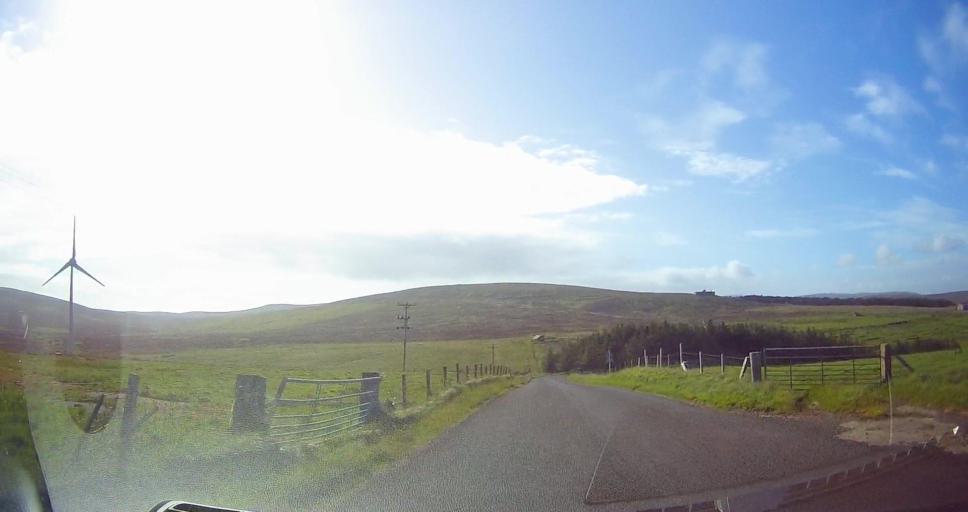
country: GB
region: Scotland
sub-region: Orkney Islands
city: Stromness
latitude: 58.8233
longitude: -3.2083
